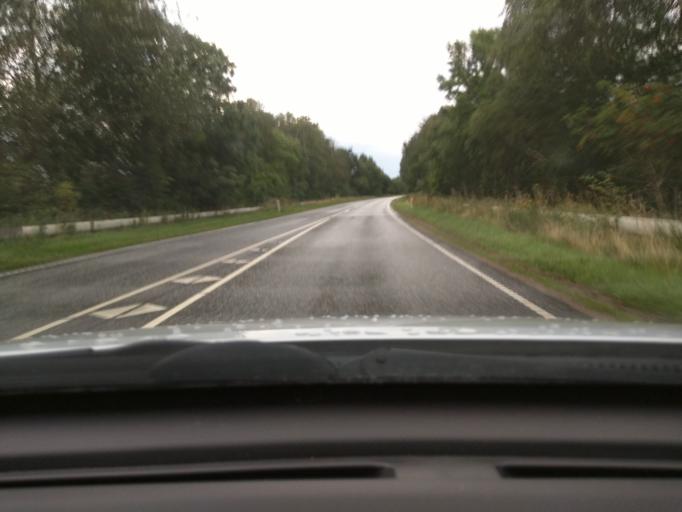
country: DK
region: Central Jutland
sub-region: Viborg Kommune
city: Viborg
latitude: 56.3870
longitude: 9.3792
